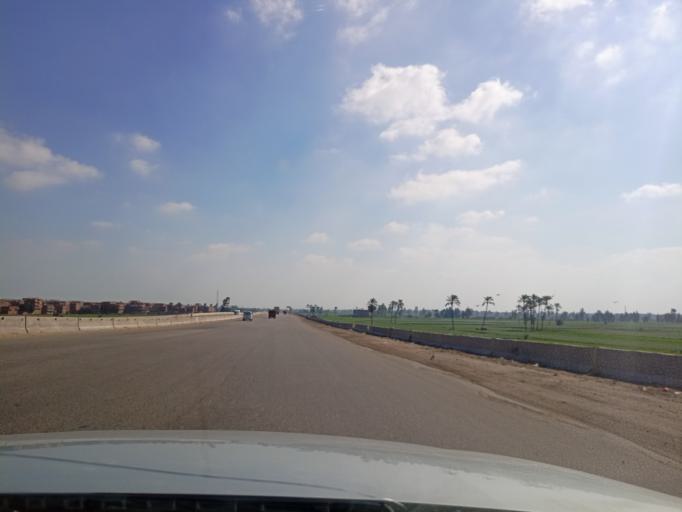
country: EG
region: Eastern Province
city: Mashtul as Suq
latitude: 30.4607
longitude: 31.3837
